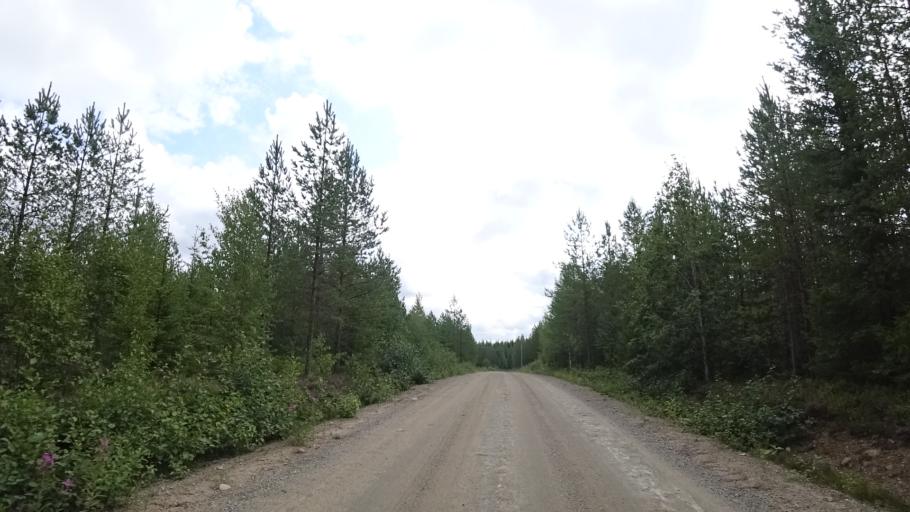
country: FI
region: North Karelia
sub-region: Joensuu
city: Ilomantsi
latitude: 62.9267
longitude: 31.3299
